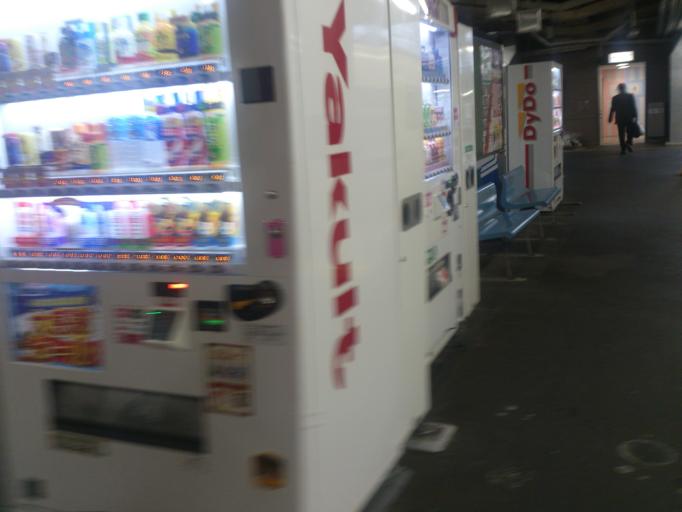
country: JP
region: Chiba
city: Matsudo
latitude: 35.7845
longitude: 139.9012
